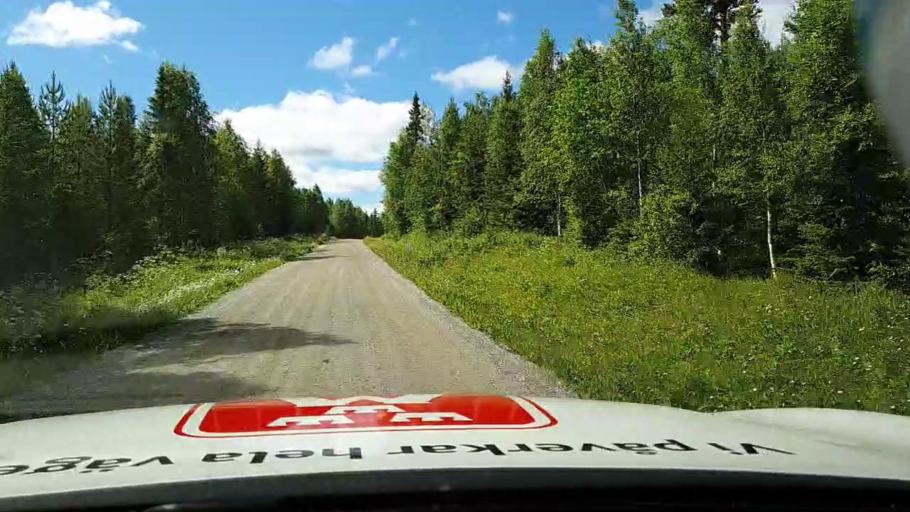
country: SE
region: Jaemtland
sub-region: Braecke Kommun
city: Braecke
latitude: 62.7436
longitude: 15.5003
